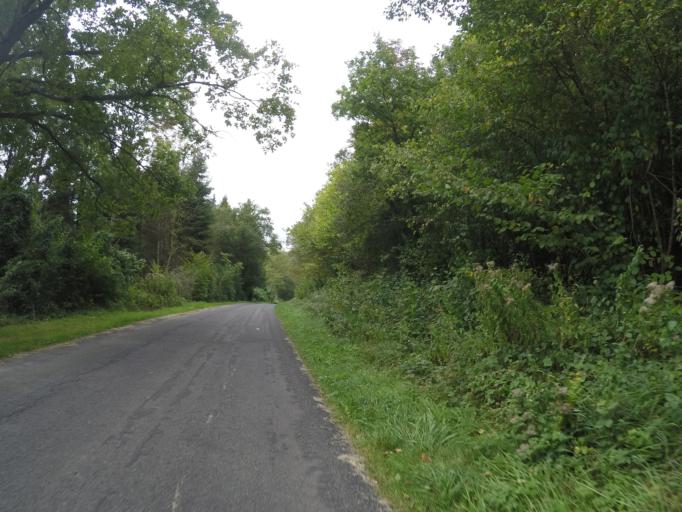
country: BE
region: Wallonia
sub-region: Province de Namur
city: Dinant
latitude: 50.2728
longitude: 4.9763
